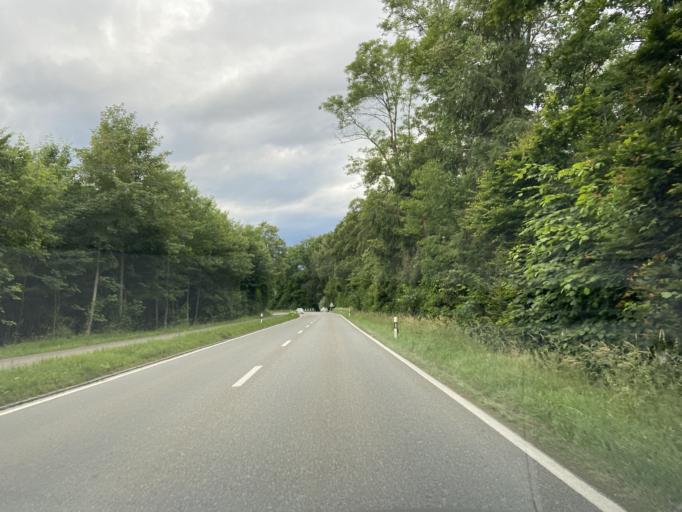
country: CH
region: Thurgau
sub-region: Muenchwilen District
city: Aadorf
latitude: 47.5003
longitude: 8.9118
